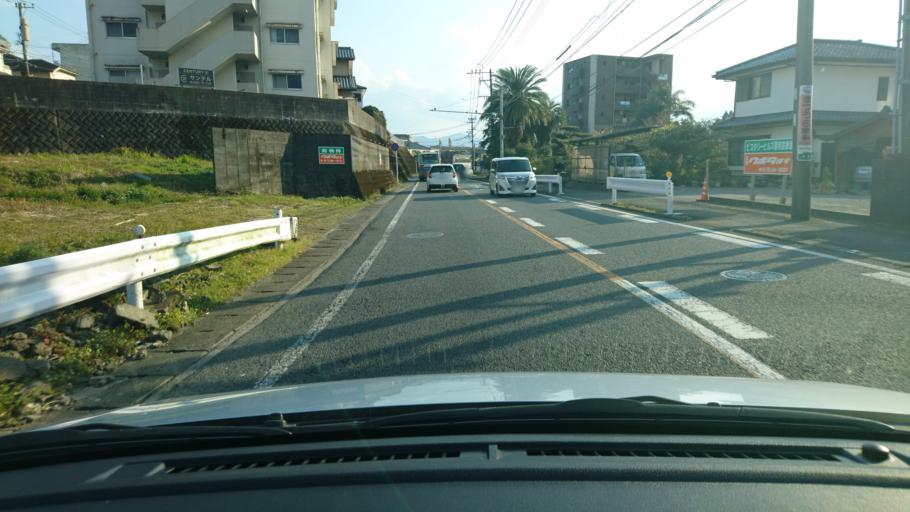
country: JP
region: Miyazaki
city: Miyazaki-shi
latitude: 31.8857
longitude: 131.4089
